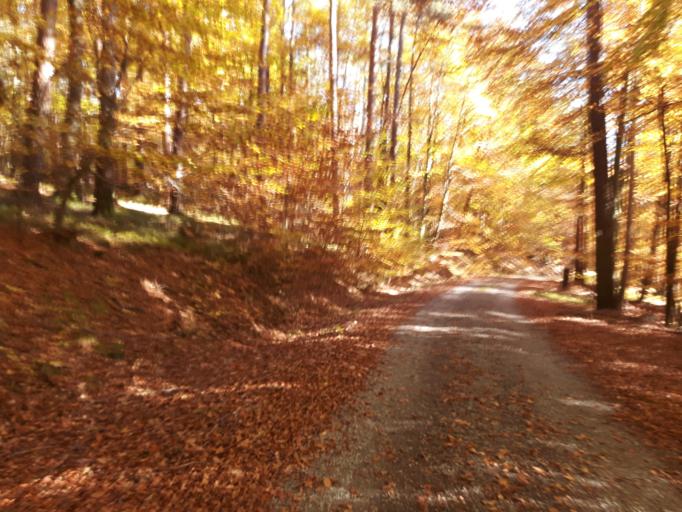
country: DE
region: Bavaria
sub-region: Regierungsbezirk Unterfranken
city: Heimbuchenthal
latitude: 49.8987
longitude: 9.2908
